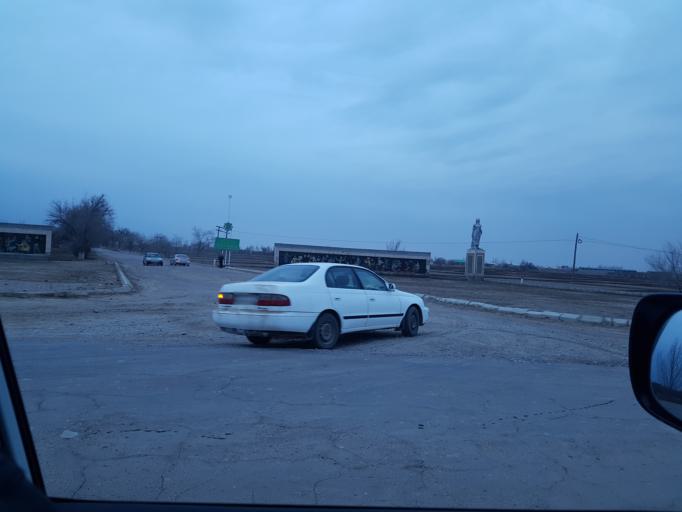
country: TM
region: Dasoguz
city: Yylanly
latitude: 41.9027
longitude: 59.6020
